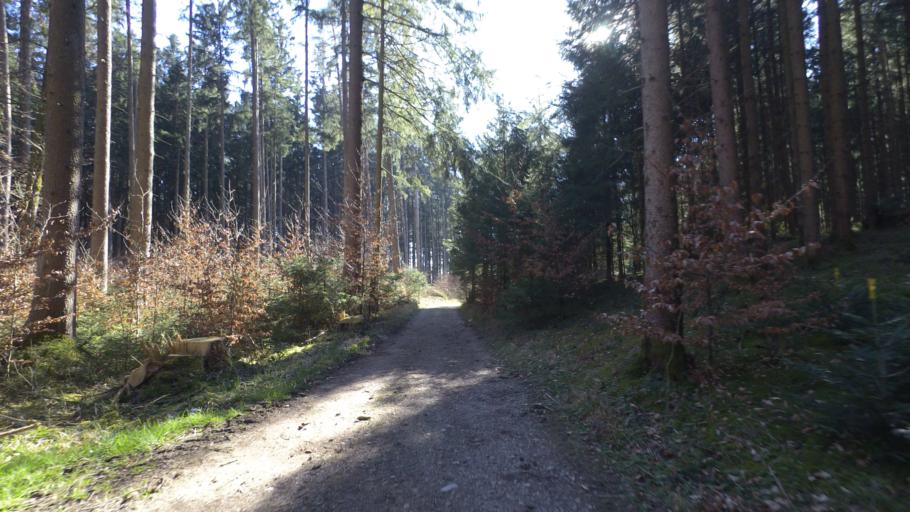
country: DE
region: Bavaria
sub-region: Upper Bavaria
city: Chieming
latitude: 47.9455
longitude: 12.5225
